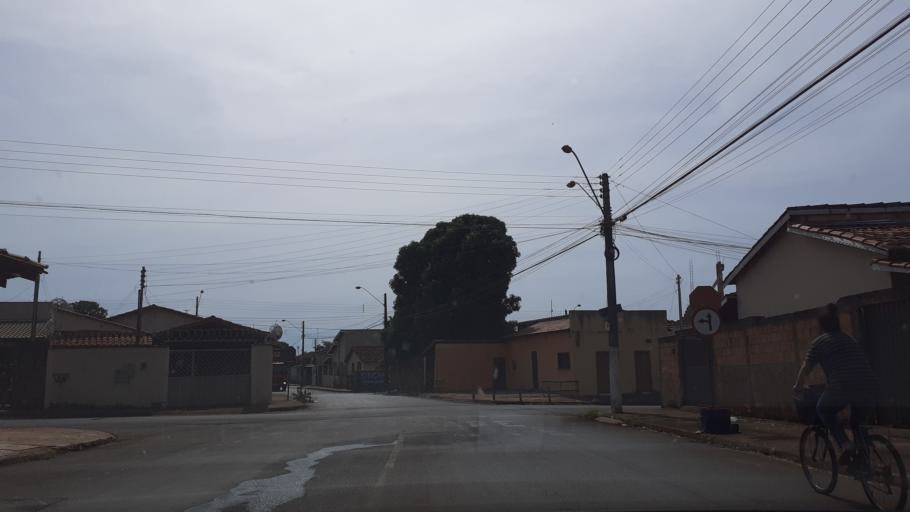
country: BR
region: Goias
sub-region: Itumbiara
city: Itumbiara
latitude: -18.4138
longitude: -49.2310
